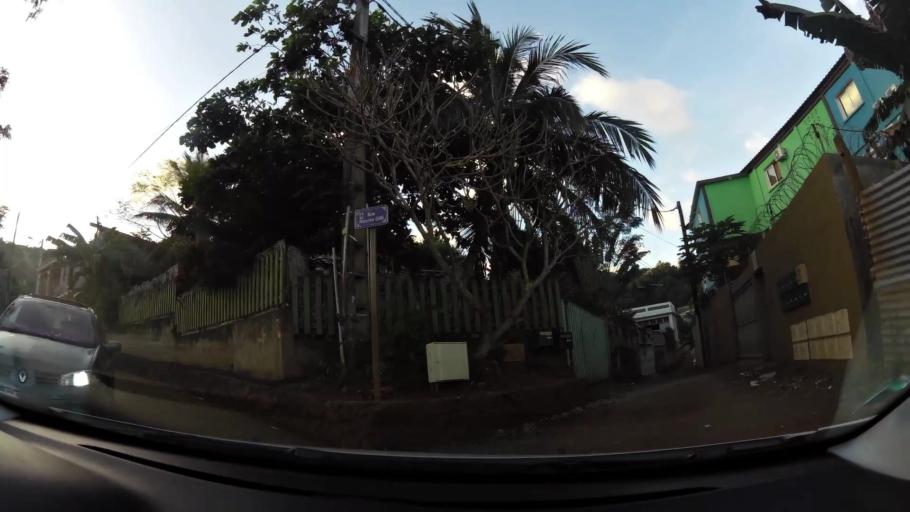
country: YT
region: Dembeni
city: Dembeni
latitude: -12.8342
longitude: 45.1707
